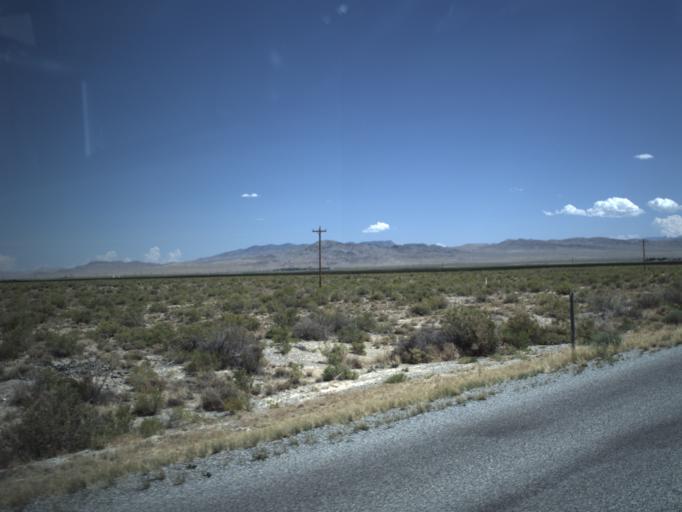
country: US
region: Nevada
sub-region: White Pine County
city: McGill
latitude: 39.0569
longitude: -114.0463
